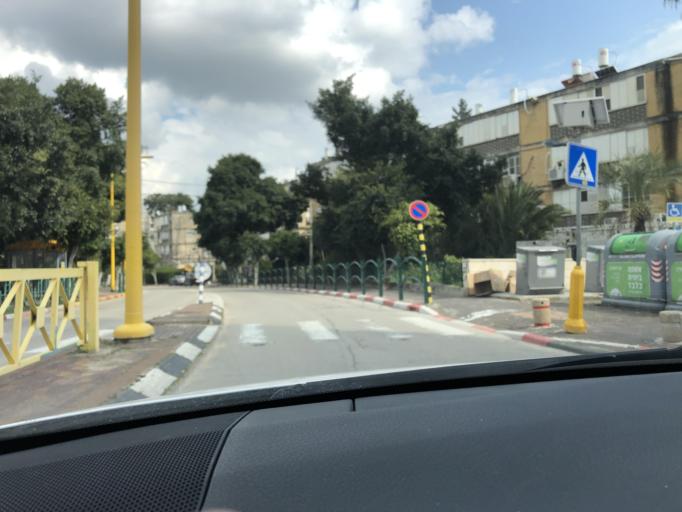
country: IL
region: Central District
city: Ganne Tiqwa
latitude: 32.0606
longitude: 34.8666
